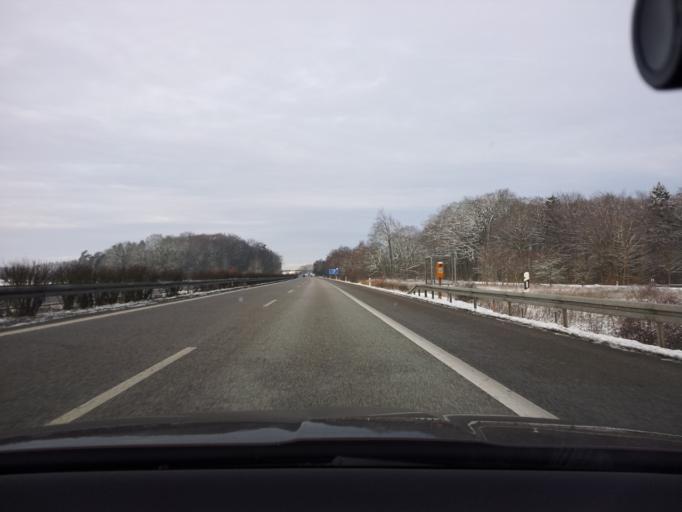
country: DE
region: Mecklenburg-Vorpommern
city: Wittenburg
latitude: 53.4935
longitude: 11.1457
